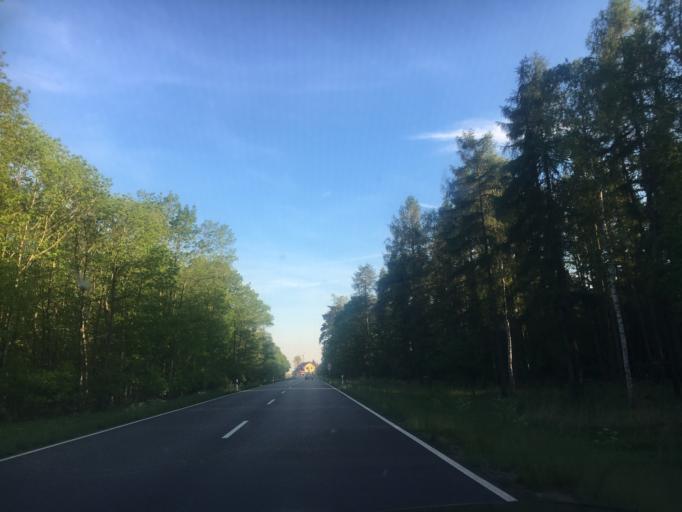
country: DE
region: Saxony-Anhalt
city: Raguhn
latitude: 51.7357
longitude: 12.2296
